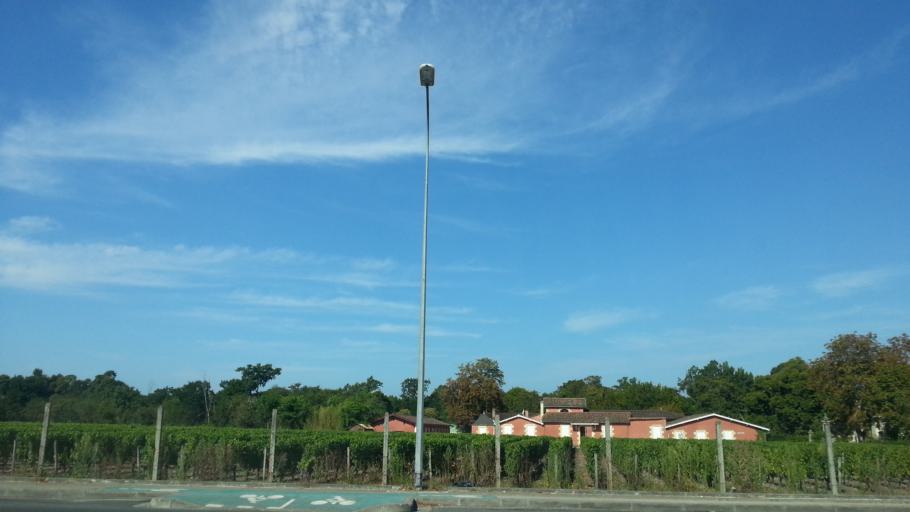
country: FR
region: Aquitaine
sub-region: Departement de la Gironde
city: Villenave-d'Ornon
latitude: 44.7724
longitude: -0.5643
